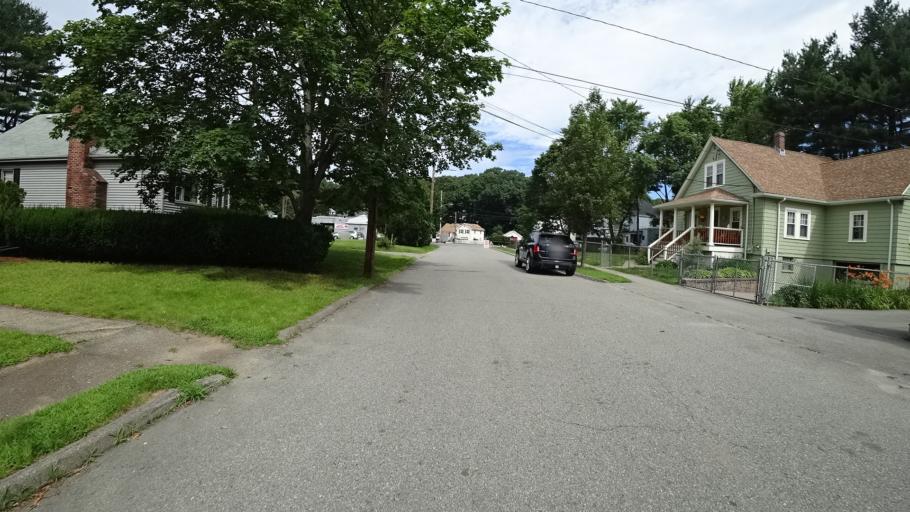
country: US
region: Massachusetts
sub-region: Norfolk County
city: Dedham
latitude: 42.2295
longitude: -71.1422
